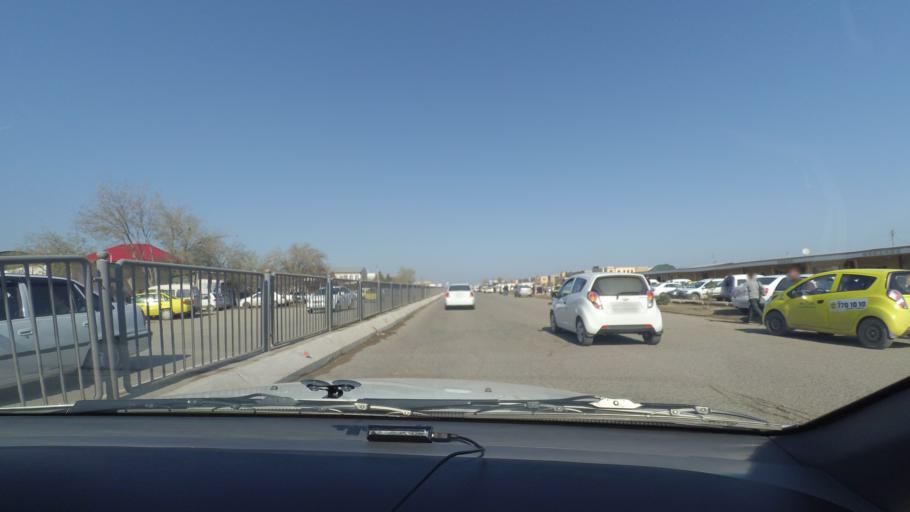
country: UZ
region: Bukhara
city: Bukhara
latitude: 39.8047
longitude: 64.4252
